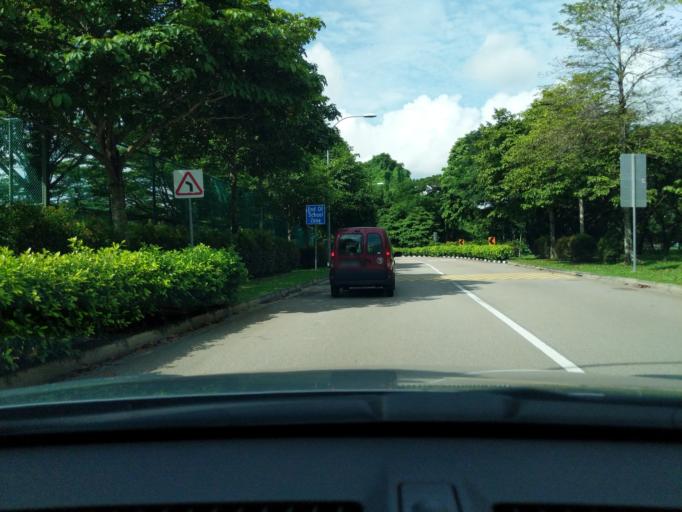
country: SG
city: Singapore
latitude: 1.2998
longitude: 103.8816
